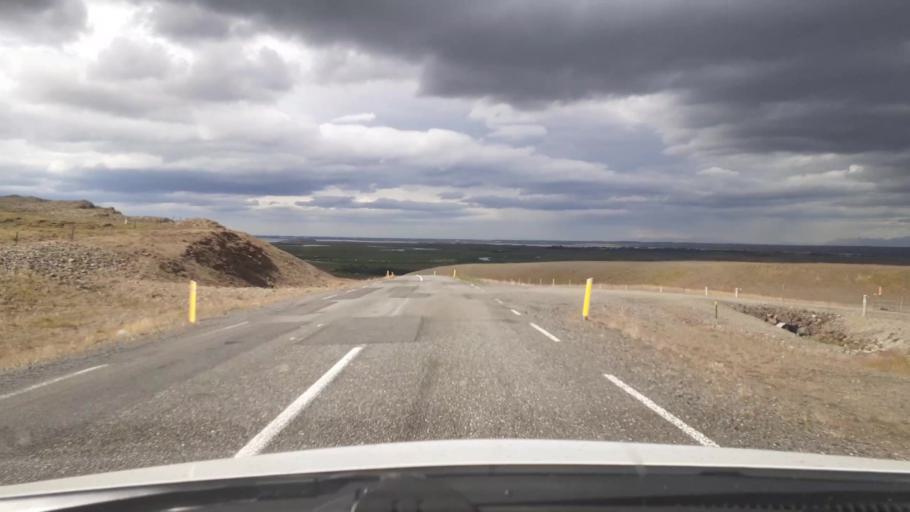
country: IS
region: West
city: Borgarnes
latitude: 64.5454
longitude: -21.6750
